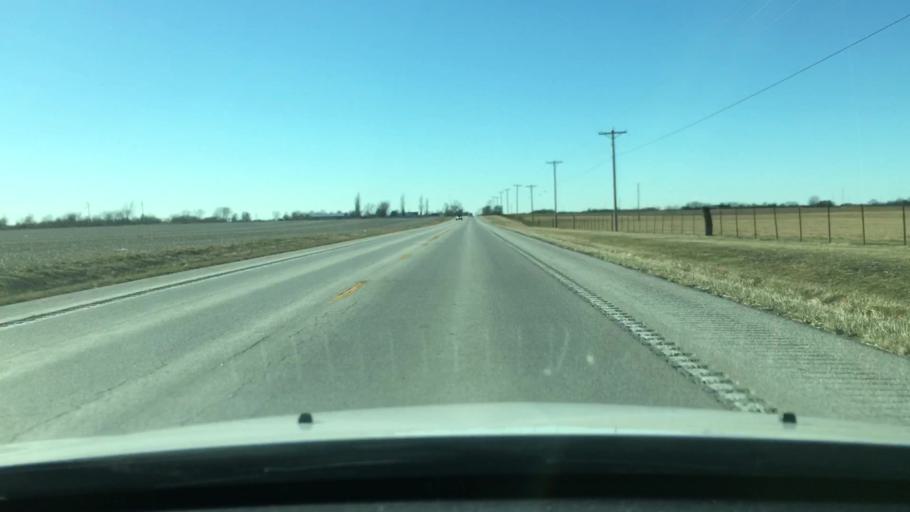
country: US
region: Missouri
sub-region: Pike County
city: Bowling Green
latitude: 39.3444
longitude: -91.2486
